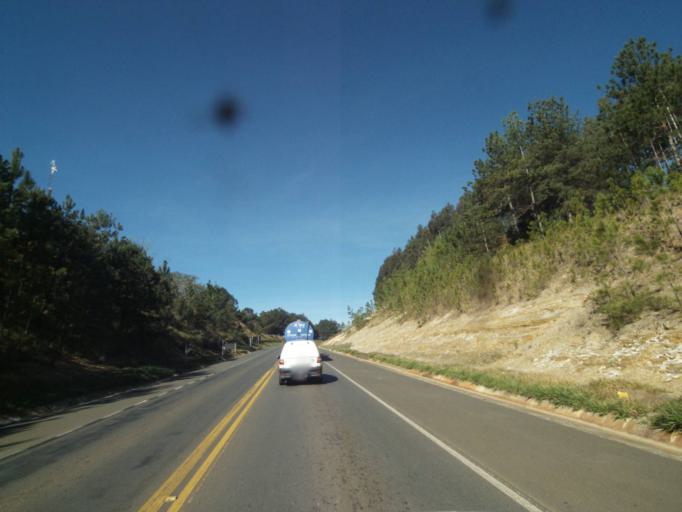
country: BR
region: Parana
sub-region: Tibagi
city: Tibagi
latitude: -24.5015
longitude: -50.4433
